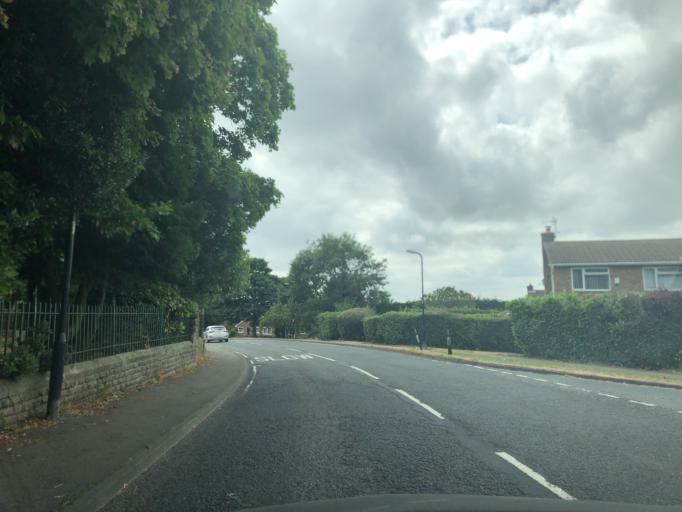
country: GB
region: England
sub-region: North Yorkshire
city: Great Ayton
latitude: 54.4931
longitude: -1.1395
